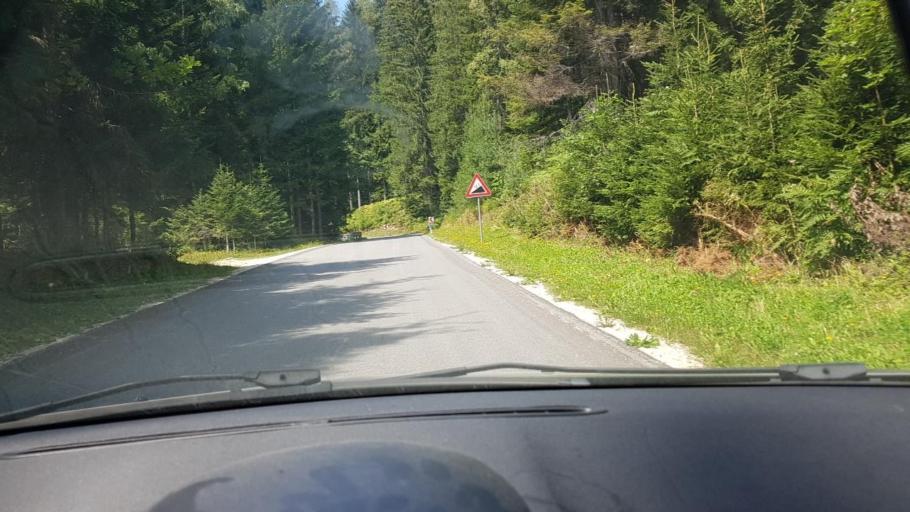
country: AT
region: Carinthia
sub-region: Politischer Bezirk Volkermarkt
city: Bad Eisenkappel
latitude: 46.4247
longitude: 14.6027
